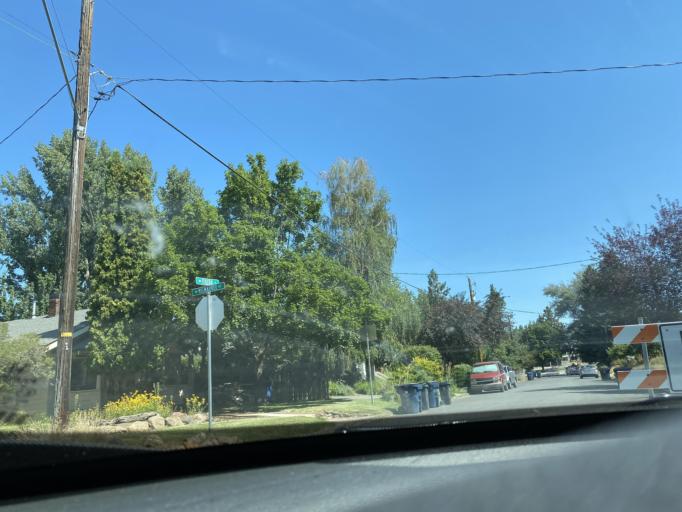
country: US
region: Oregon
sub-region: Deschutes County
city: Bend
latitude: 44.0610
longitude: -121.3253
